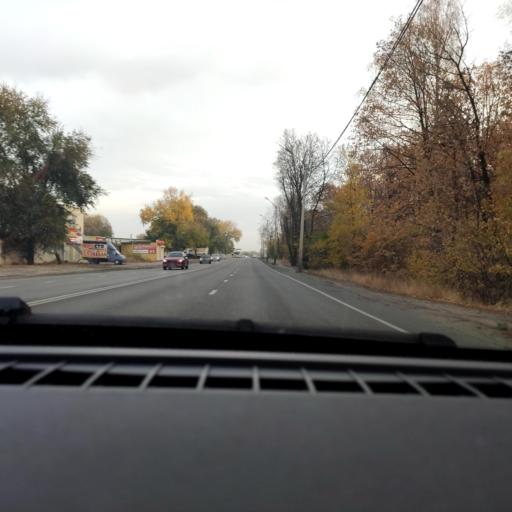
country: RU
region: Voronezj
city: Voronezh
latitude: 51.6688
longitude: 39.2714
